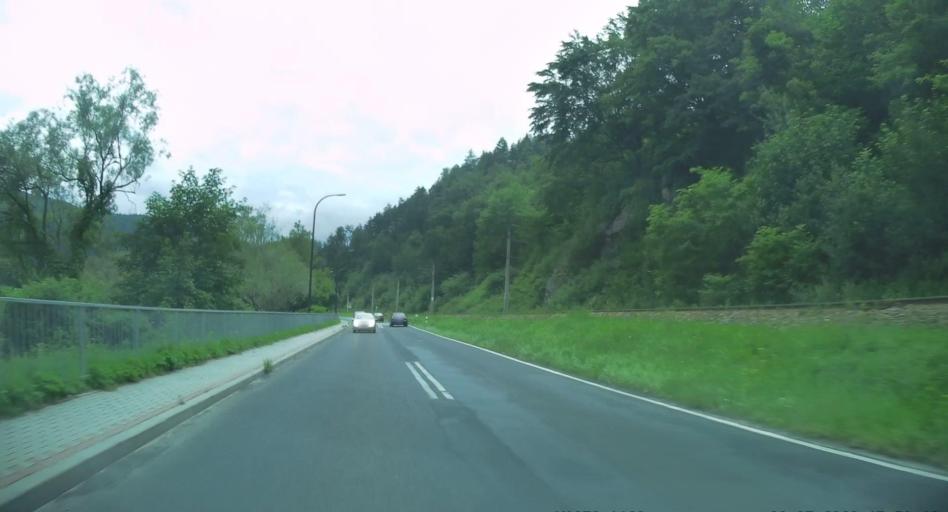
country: PL
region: Lesser Poland Voivodeship
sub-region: Powiat nowosadecki
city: Muszyna
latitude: 49.3636
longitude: 20.7978
